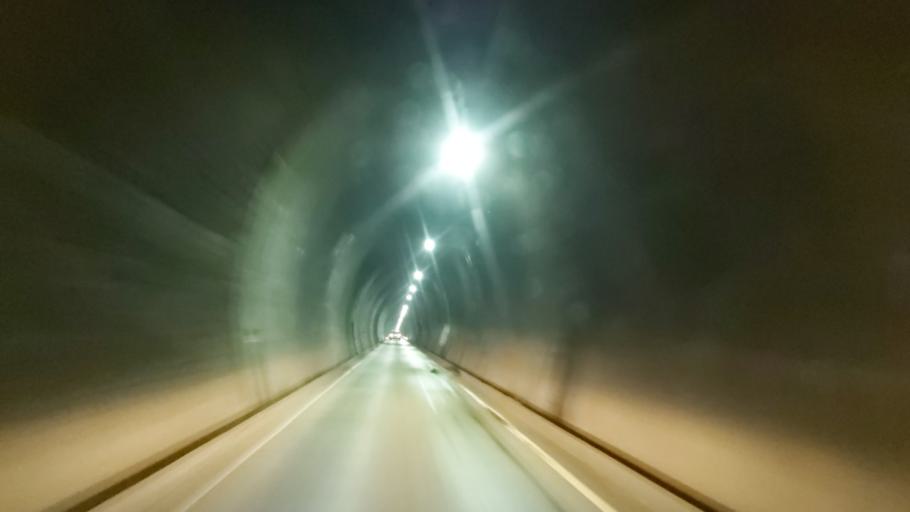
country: CL
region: Araucania
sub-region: Provincia de Cautin
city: Vilcun
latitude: -38.5397
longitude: -71.5066
